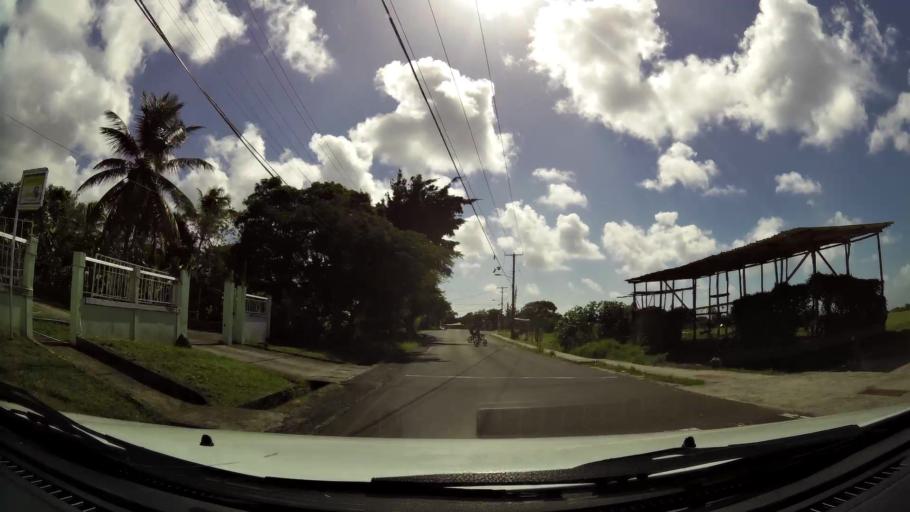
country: LC
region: Choiseul Quarter
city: Choiseul
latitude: 13.7574
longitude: -61.0221
